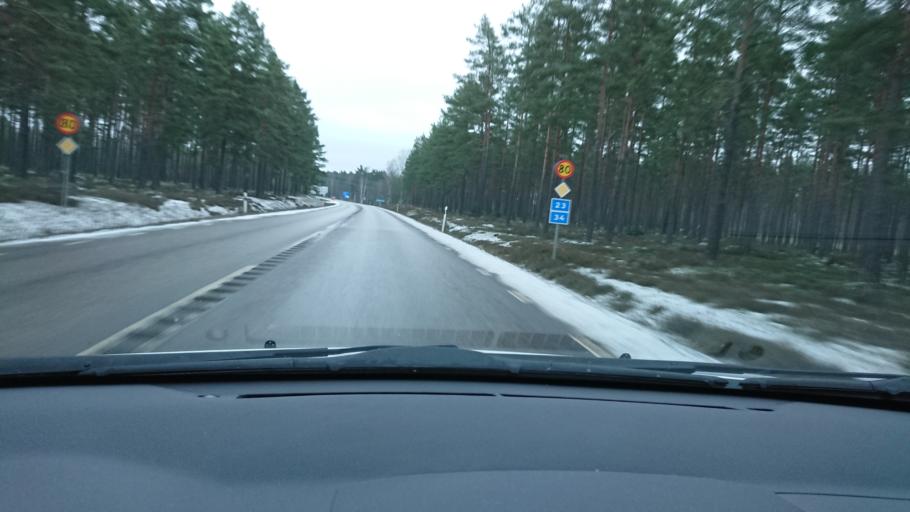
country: SE
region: Kalmar
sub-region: Hultsfreds Kommun
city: Hultsfred
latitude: 57.5115
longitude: 15.8372
